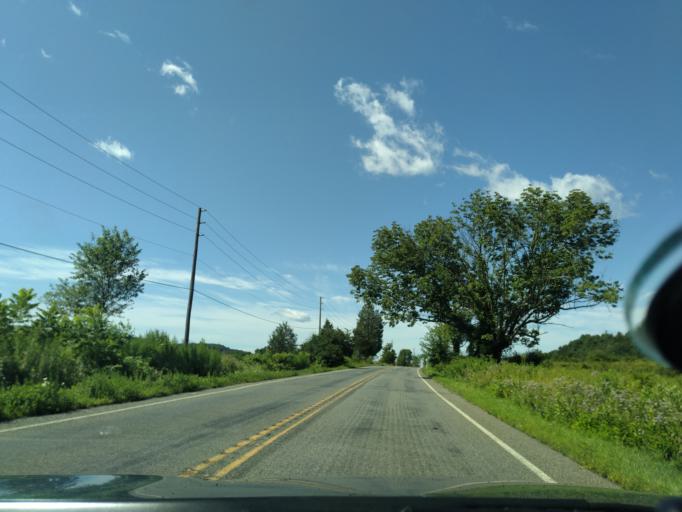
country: US
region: Pennsylvania
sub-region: Pike County
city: Pocono Ranch Lands
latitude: 41.1239
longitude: -74.9549
